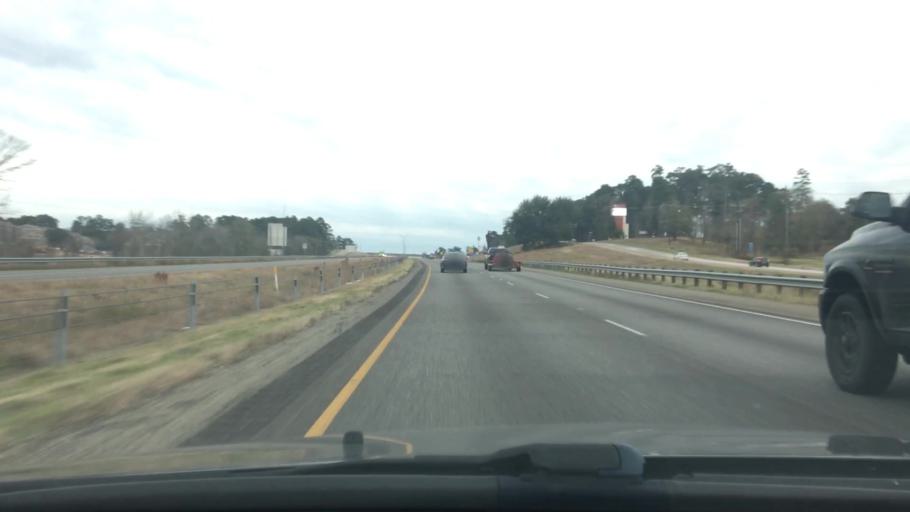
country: US
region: Texas
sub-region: Walker County
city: Huntsville
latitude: 30.7024
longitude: -95.5593
